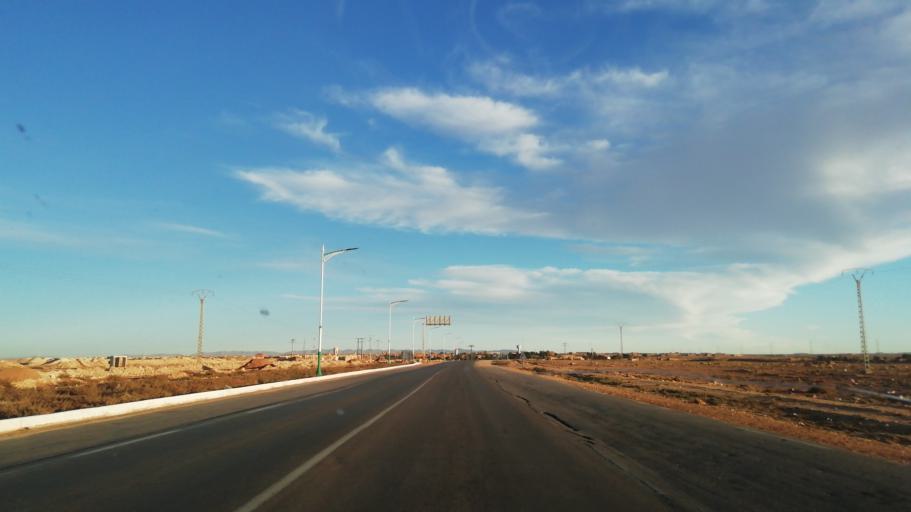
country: DZ
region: Wilaya de Naama
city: Naama
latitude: 33.7250
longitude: -0.7416
